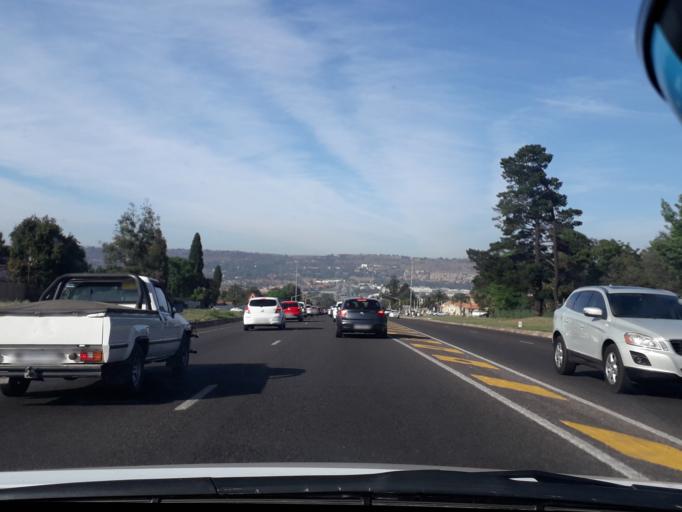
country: ZA
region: Gauteng
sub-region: City of Johannesburg Metropolitan Municipality
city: Roodepoort
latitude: -26.1109
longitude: 27.9202
